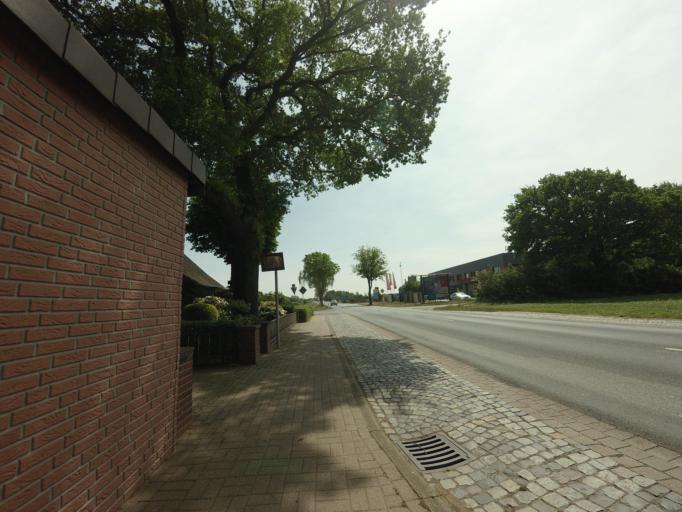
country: DE
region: Lower Saxony
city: Klein Schwulper
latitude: 52.3295
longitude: 10.4652
